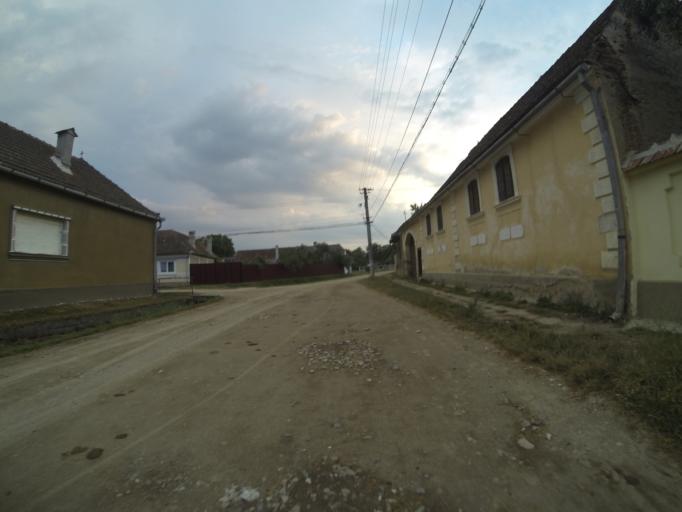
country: RO
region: Brasov
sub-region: Comuna Sinca Veche
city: Sinca Veche
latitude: 45.7646
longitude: 25.1728
